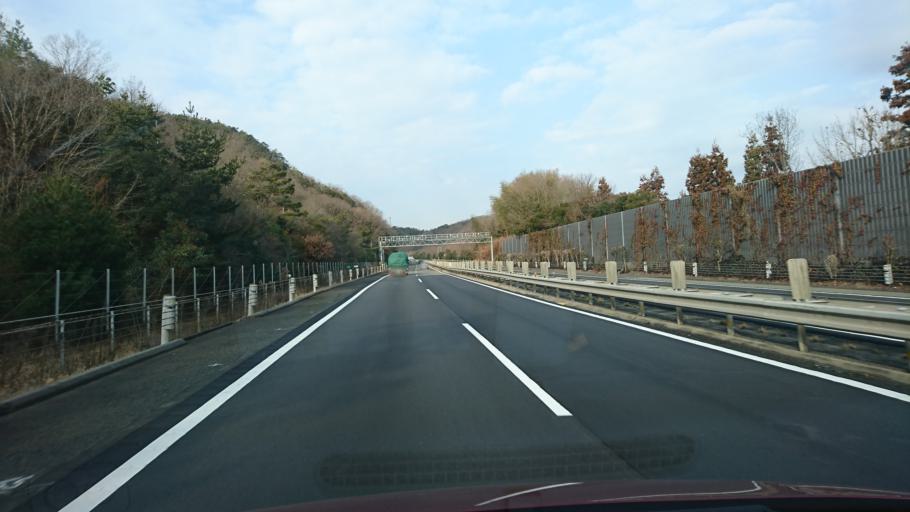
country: JP
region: Hyogo
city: Kariya
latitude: 34.7821
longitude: 134.2860
